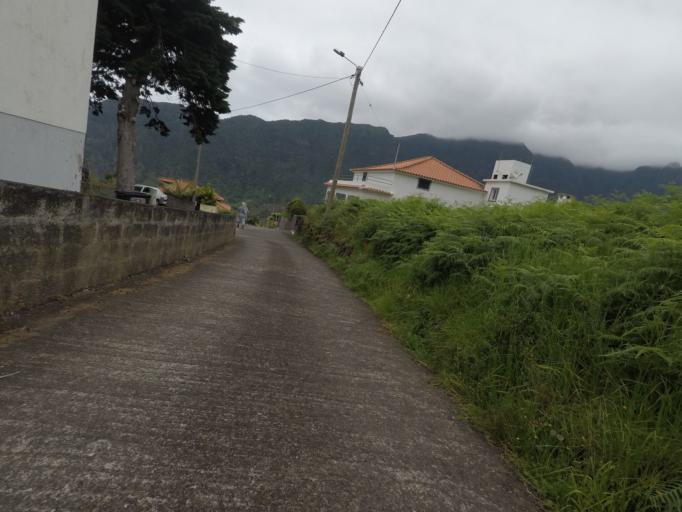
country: PT
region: Madeira
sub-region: Sao Vicente
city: Sao Vicente
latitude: 32.7853
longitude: -17.0429
